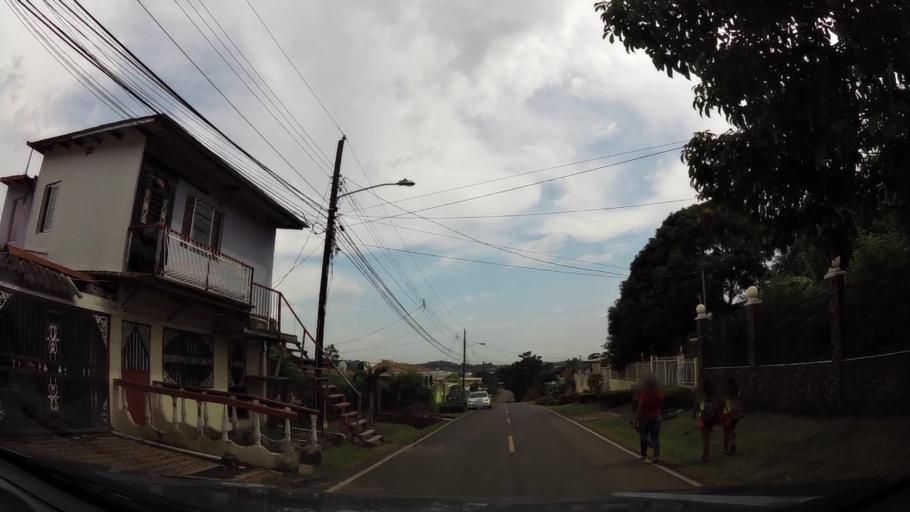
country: PA
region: Panama
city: Tocumen
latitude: 9.1111
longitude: -79.3743
